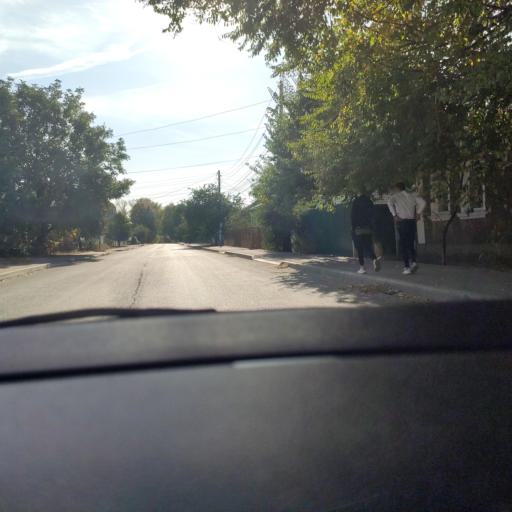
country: RU
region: Voronezj
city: Voronezh
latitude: 51.6810
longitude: 39.1405
